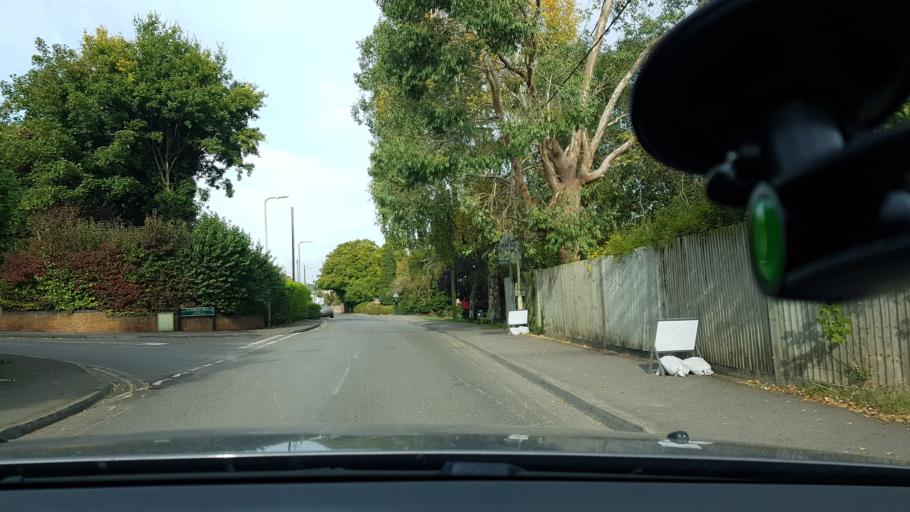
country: GB
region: England
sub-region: West Berkshire
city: Hungerford
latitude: 51.4133
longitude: -1.5104
